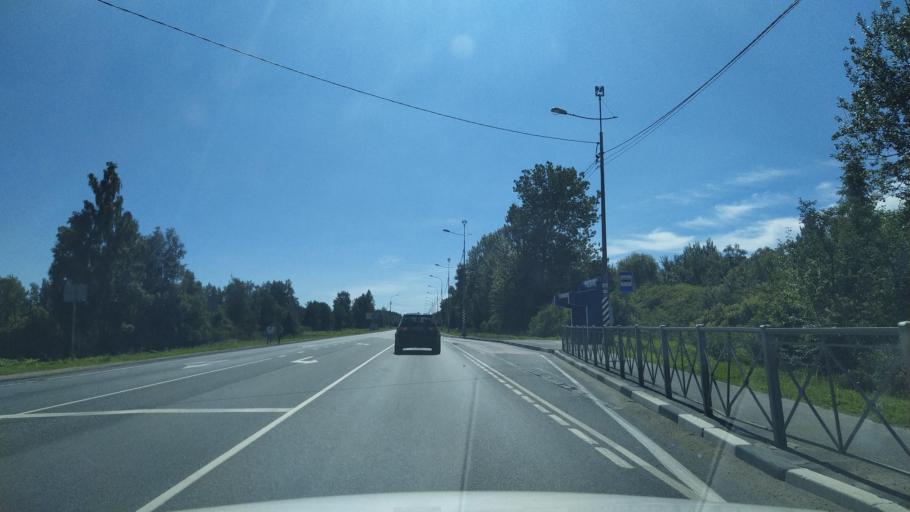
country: RU
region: Pskov
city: Pskov
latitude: 57.7899
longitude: 28.4123
